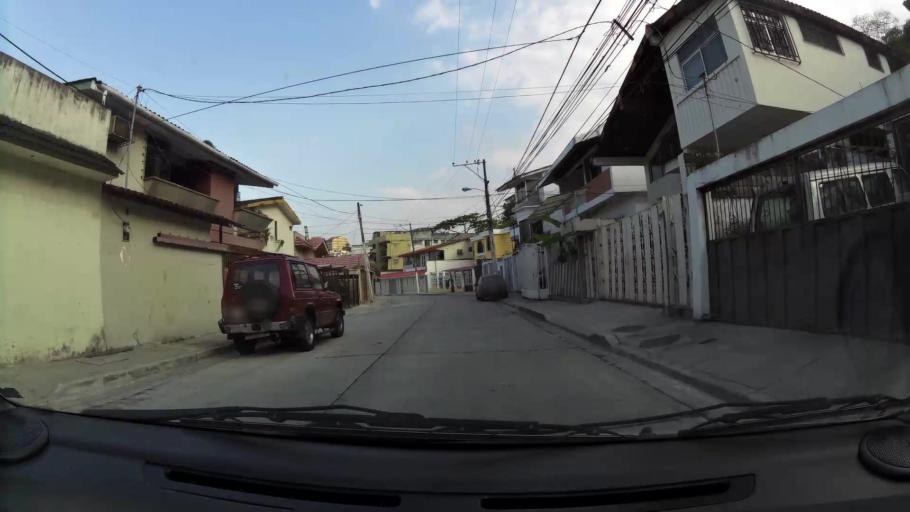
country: EC
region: Guayas
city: Guayaquil
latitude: -2.1584
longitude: -79.9077
